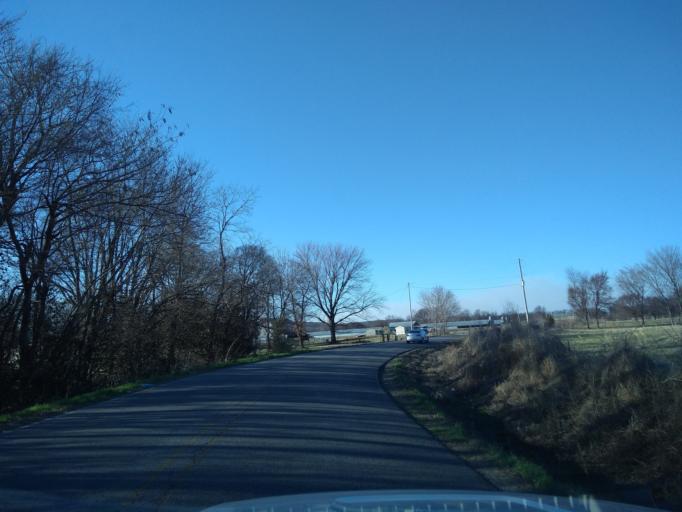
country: US
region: Arkansas
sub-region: Washington County
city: Lincoln
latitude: 36.0165
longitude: -94.3929
